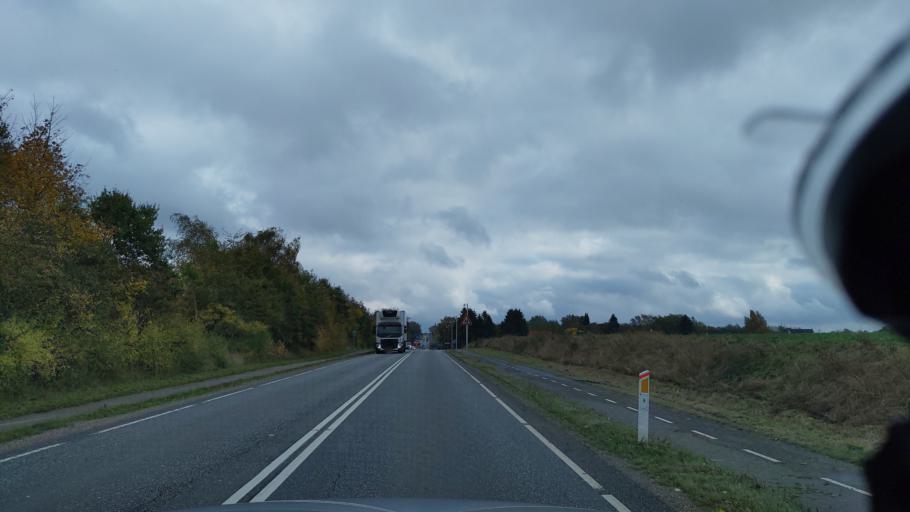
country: DK
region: Zealand
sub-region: Naestved Kommune
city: Fensmark
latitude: 55.2586
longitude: 11.8677
